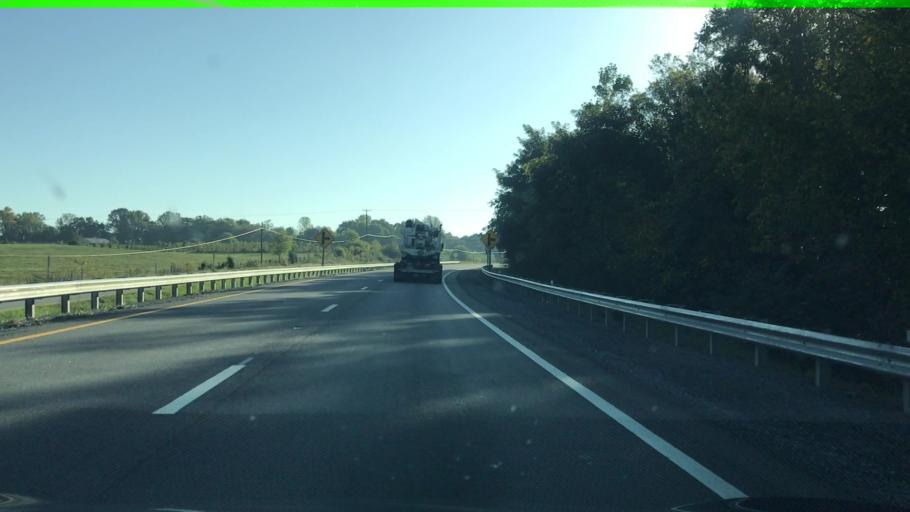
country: US
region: Virginia
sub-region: City of Bedford
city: Bedford
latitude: 37.3191
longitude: -79.4354
